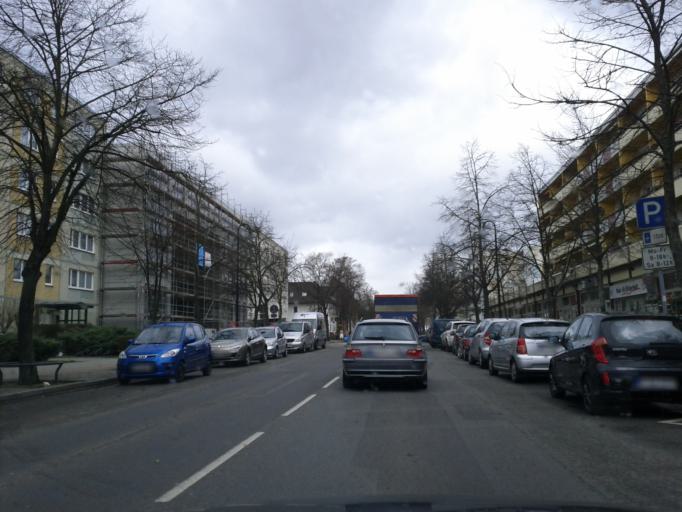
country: DE
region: Brandenburg
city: Erkner
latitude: 52.4223
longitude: 13.7532
